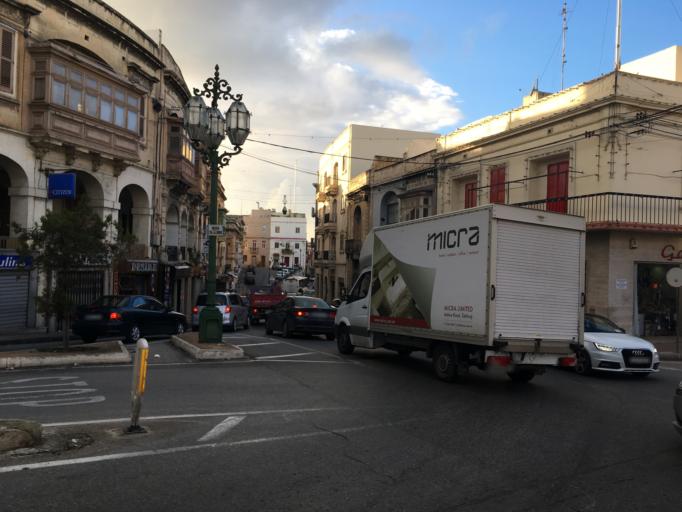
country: MT
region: Birkirkara
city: Birkirkara
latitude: 35.8961
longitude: 14.4646
